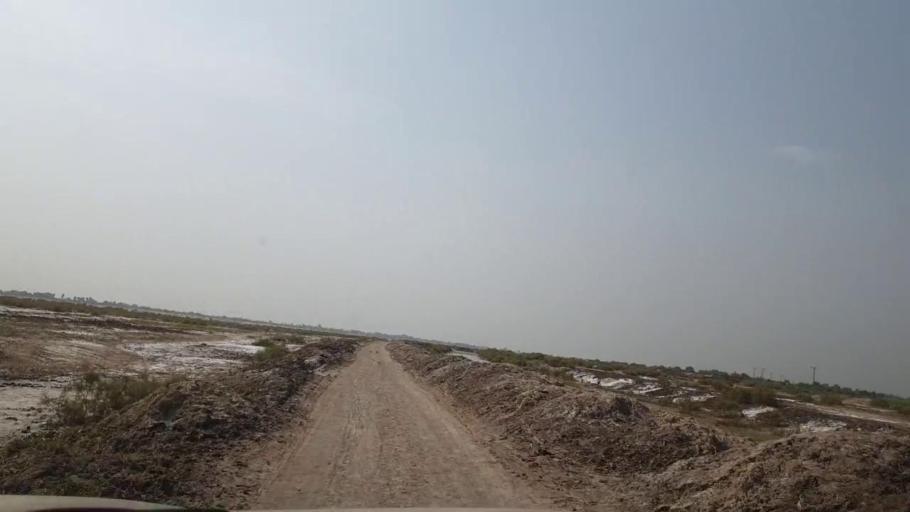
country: PK
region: Sindh
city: Dokri
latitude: 27.4232
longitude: 68.2046
